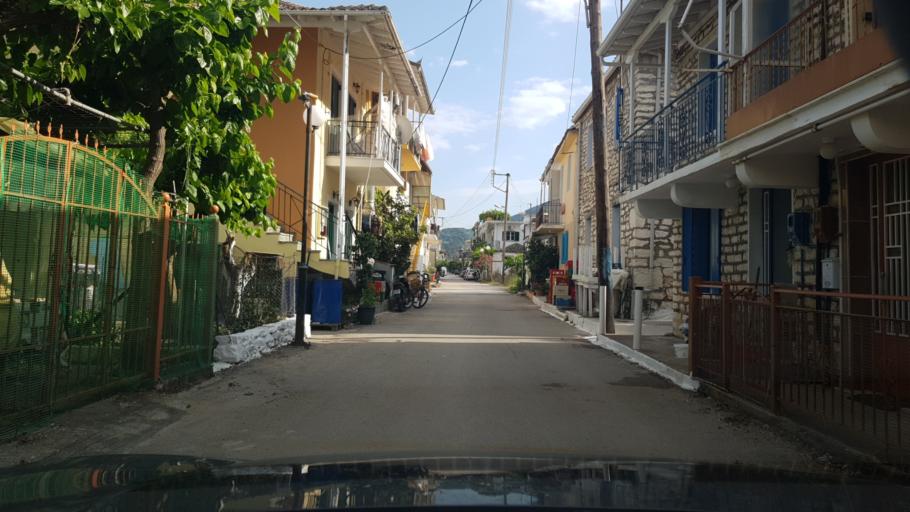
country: GR
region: Ionian Islands
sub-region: Lefkada
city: Nidri
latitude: 38.6881
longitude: 20.6984
